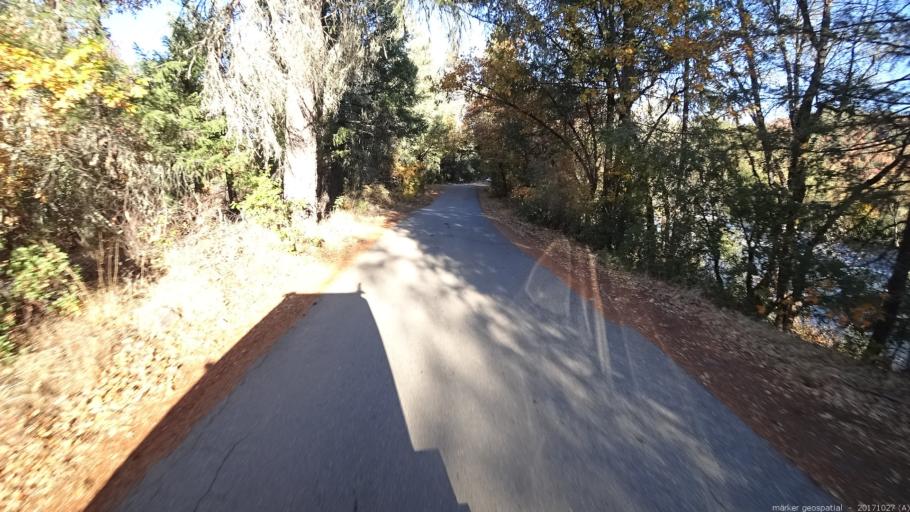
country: US
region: California
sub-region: Shasta County
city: Burney
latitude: 41.0204
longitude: -121.9142
